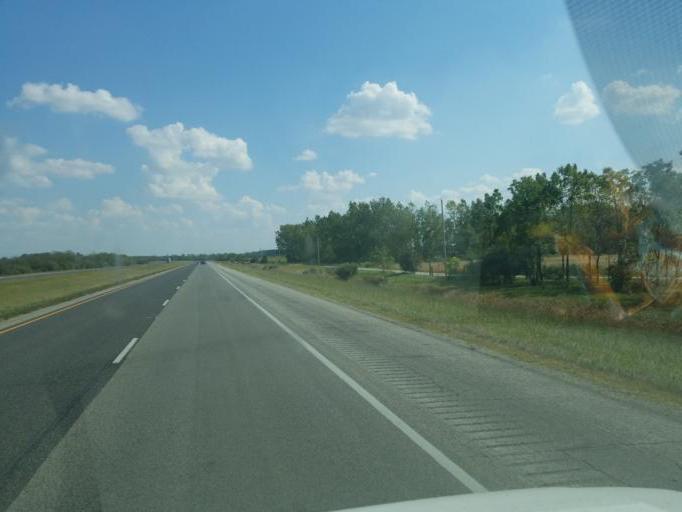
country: US
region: Indiana
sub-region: Allen County
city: Monroeville
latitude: 41.0040
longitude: -84.8357
